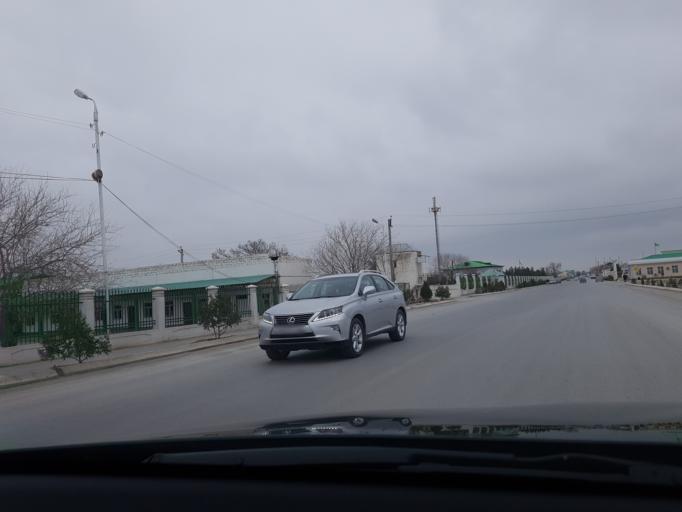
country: TM
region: Ahal
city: Abadan
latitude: 38.1455
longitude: 57.9536
